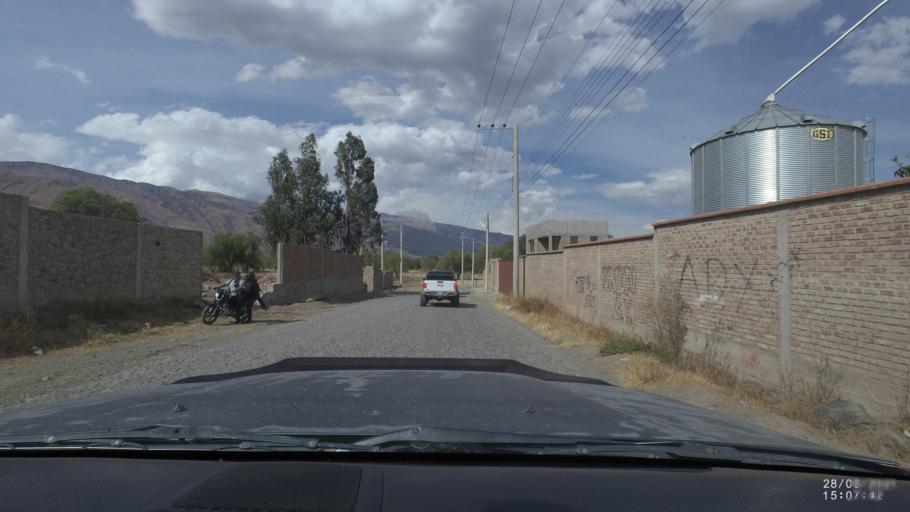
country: BO
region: Cochabamba
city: Cochabamba
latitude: -17.3367
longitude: -66.2799
